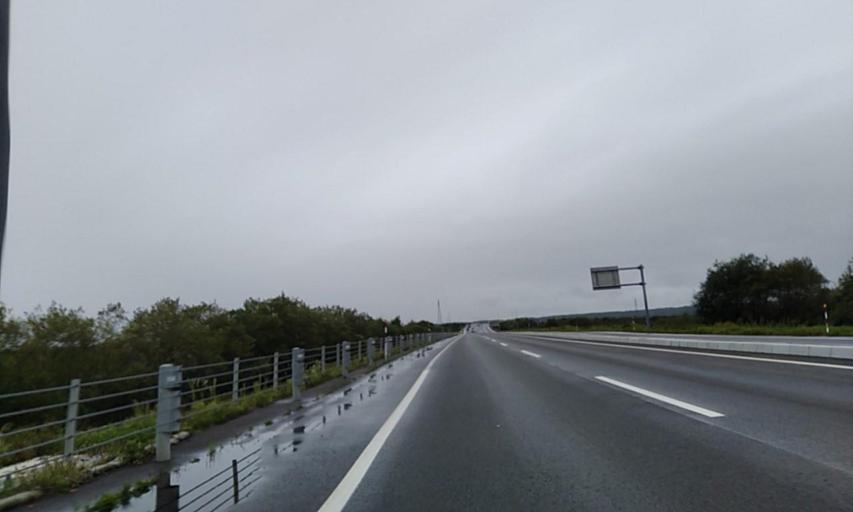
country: JP
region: Hokkaido
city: Kushiro
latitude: 43.0261
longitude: 144.2889
